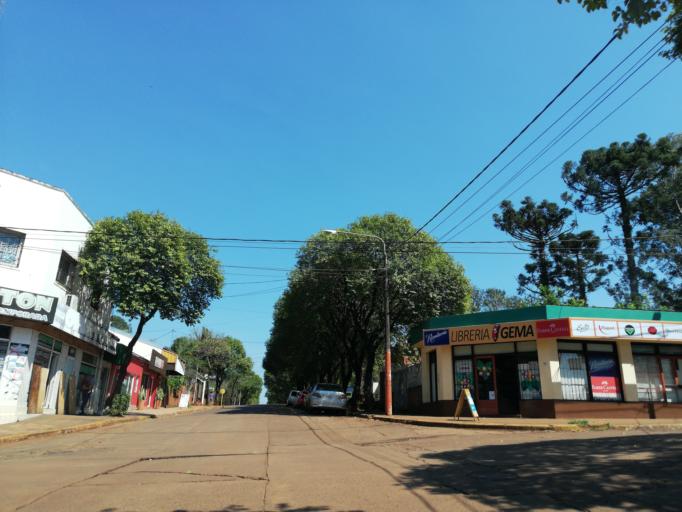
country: AR
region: Misiones
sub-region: Departamento de Eldorado
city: Eldorado
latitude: -26.4109
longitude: -54.6068
